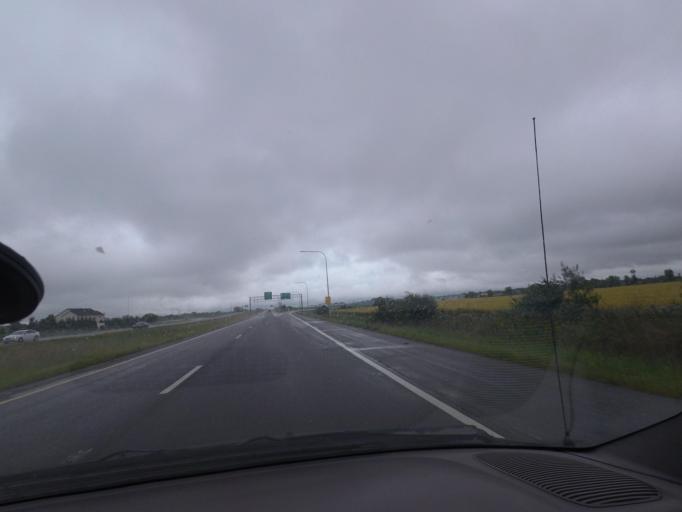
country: US
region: Illinois
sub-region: Champaign County
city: Champaign
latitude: 40.1200
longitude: -88.3116
